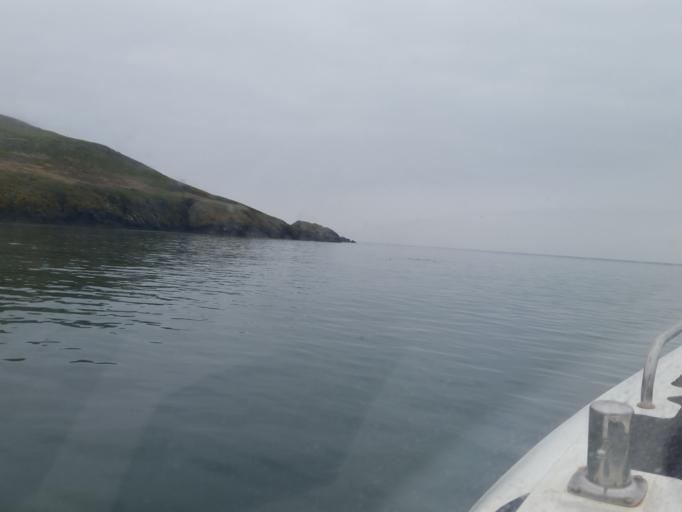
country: IE
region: Leinster
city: Portraine
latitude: 53.4810
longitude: -6.0188
